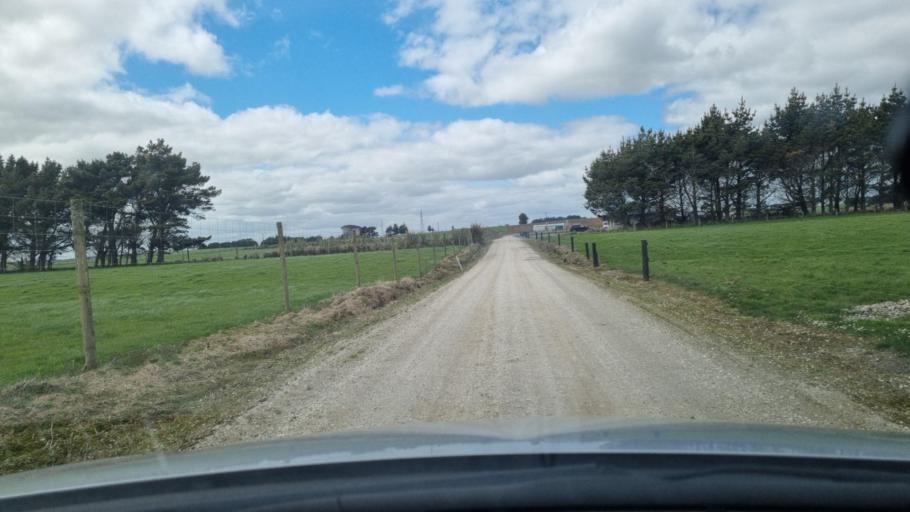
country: NZ
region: Southland
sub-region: Invercargill City
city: Invercargill
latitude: -46.4557
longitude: 168.4248
